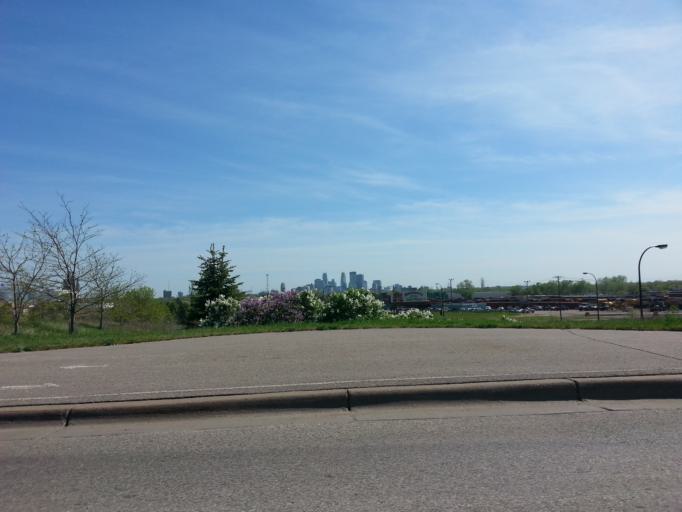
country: US
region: Minnesota
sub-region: Anoka County
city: Columbia Heights
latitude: 45.0276
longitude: -93.2633
